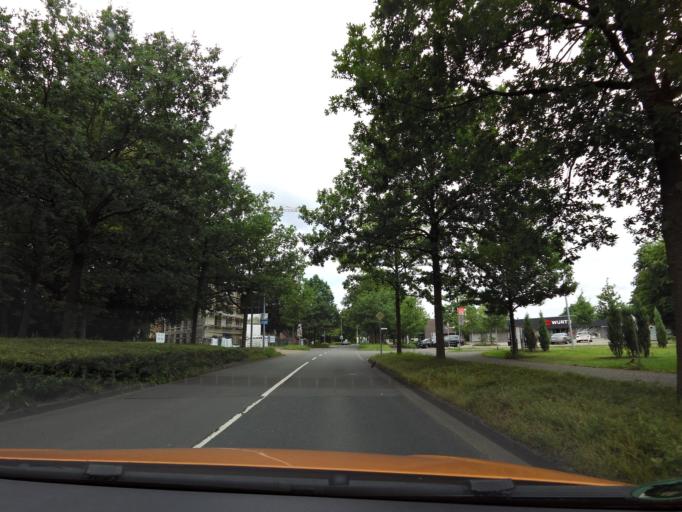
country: DE
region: Lower Saxony
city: Oldenburg
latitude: 53.1534
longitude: 8.1727
